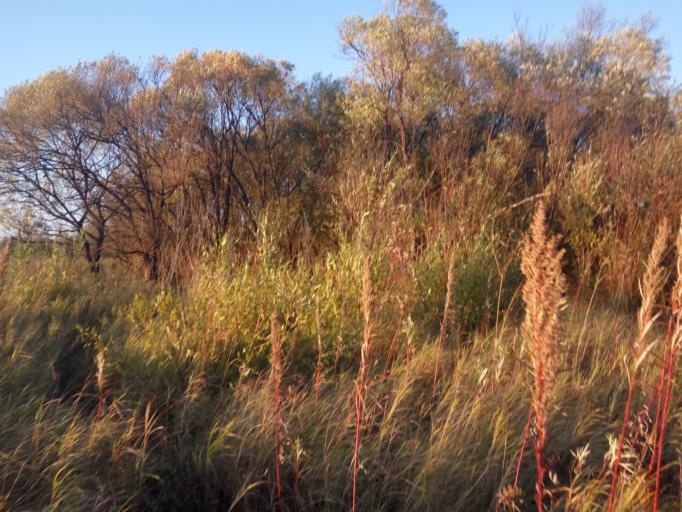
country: RU
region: Khabarovsk Krai
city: Khor
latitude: 47.7031
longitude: 134.9643
